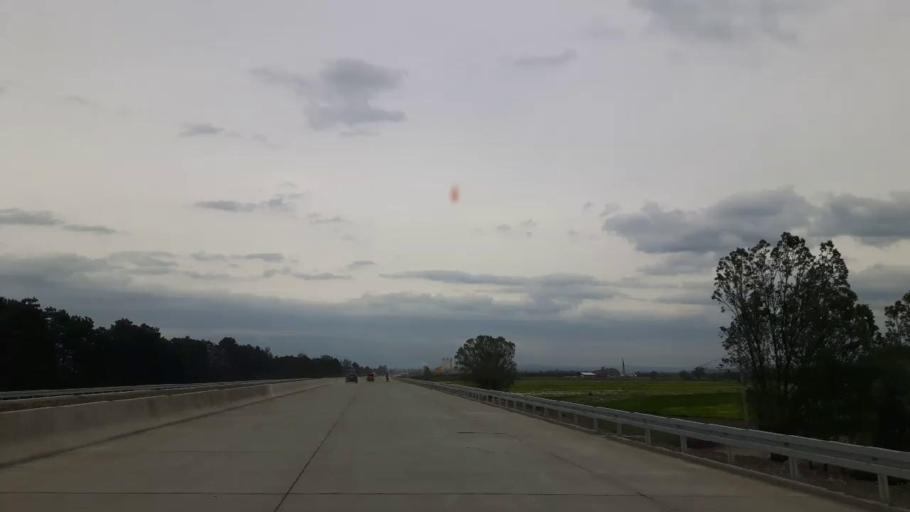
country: GE
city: Agara
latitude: 42.0263
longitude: 43.7663
